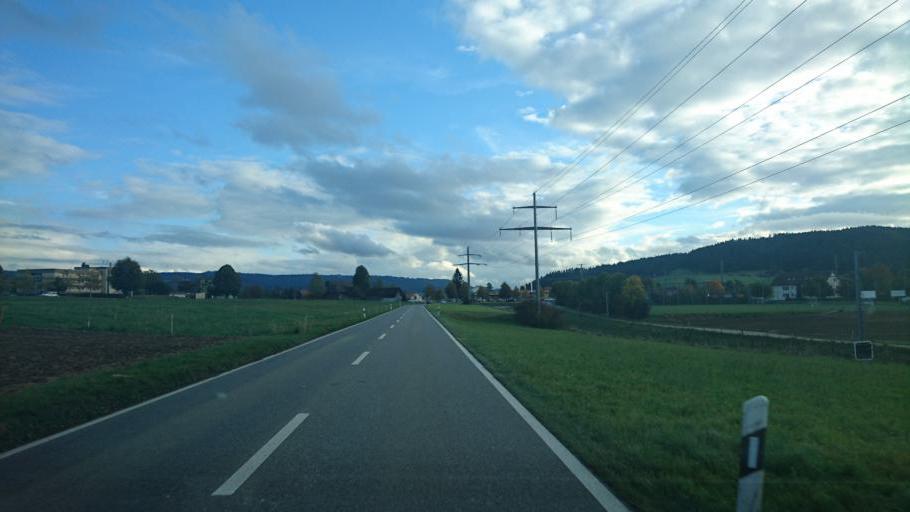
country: CH
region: Bern
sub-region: Bern-Mittelland District
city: Biglen
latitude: 46.9130
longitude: 7.6326
